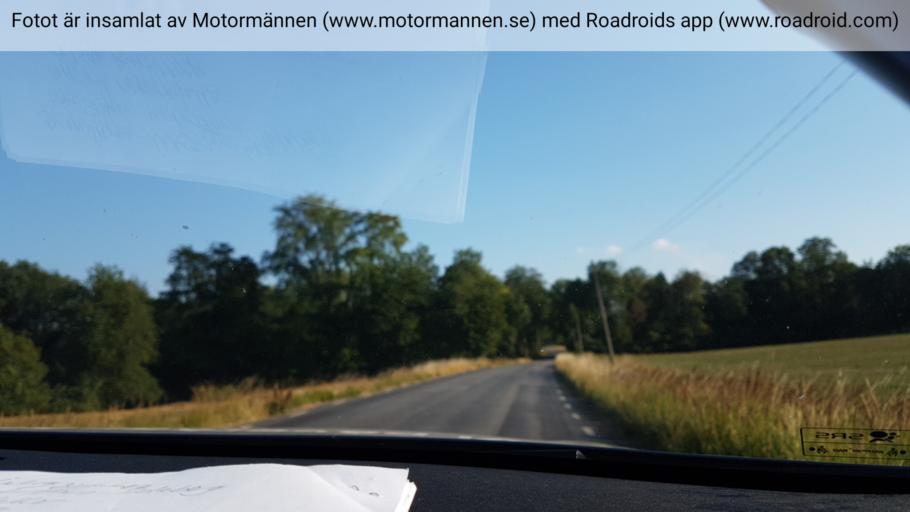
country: SE
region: Vaestra Goetaland
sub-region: Skovde Kommun
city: Stopen
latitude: 58.4627
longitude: 13.8410
